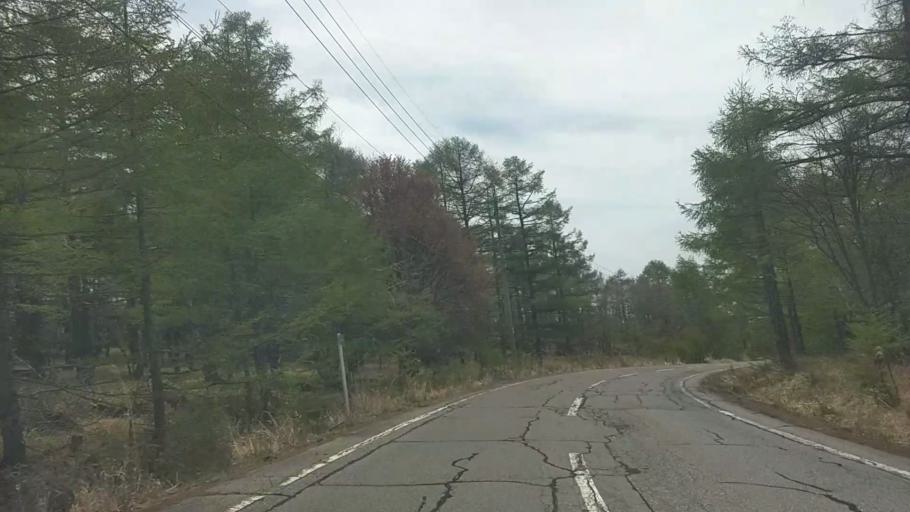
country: JP
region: Nagano
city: Chino
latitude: 36.0524
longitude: 138.3109
